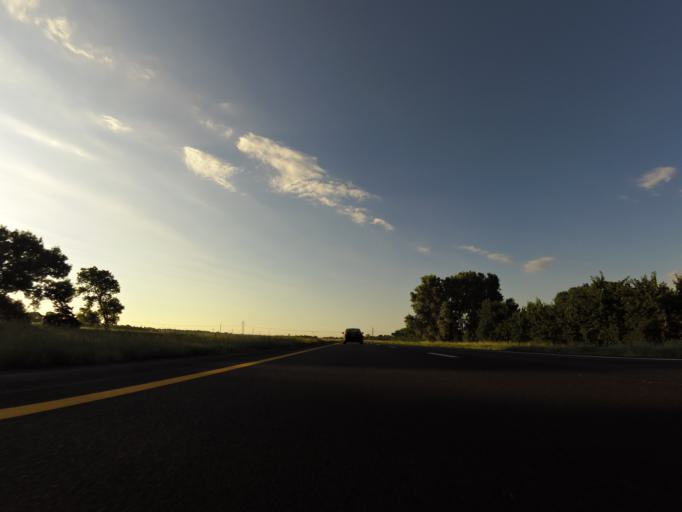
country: US
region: Kansas
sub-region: Sedgwick County
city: Colwich
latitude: 37.8114
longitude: -97.5027
